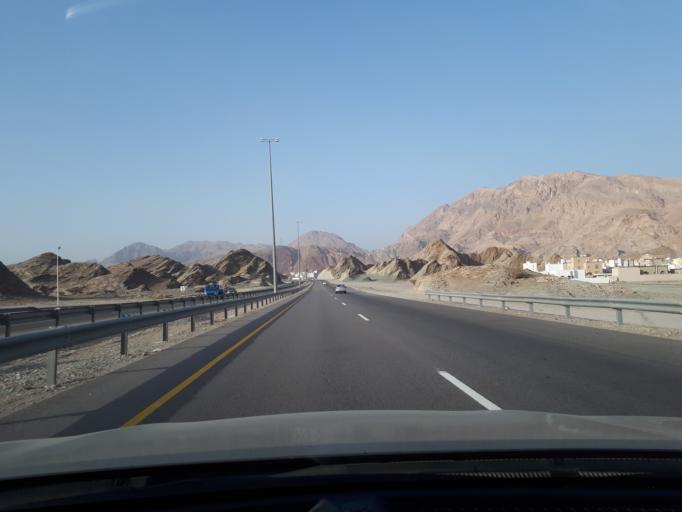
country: OM
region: Muhafazat Masqat
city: Bawshar
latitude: 23.4321
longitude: 58.5068
